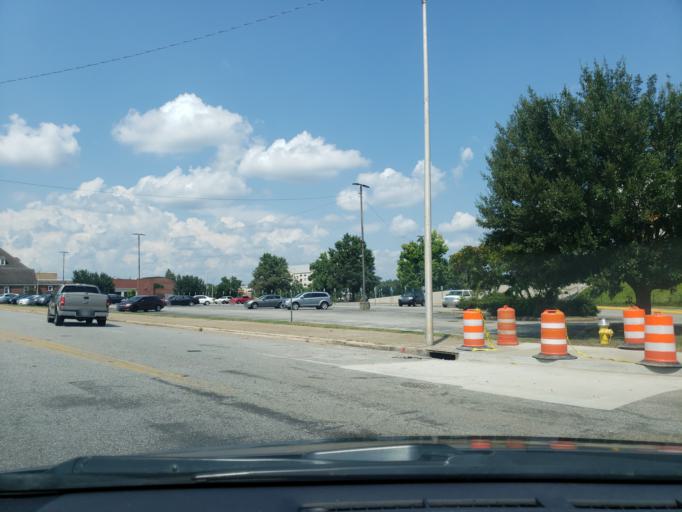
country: US
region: Georgia
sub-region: Dougherty County
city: Albany
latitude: 31.5738
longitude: -84.1514
